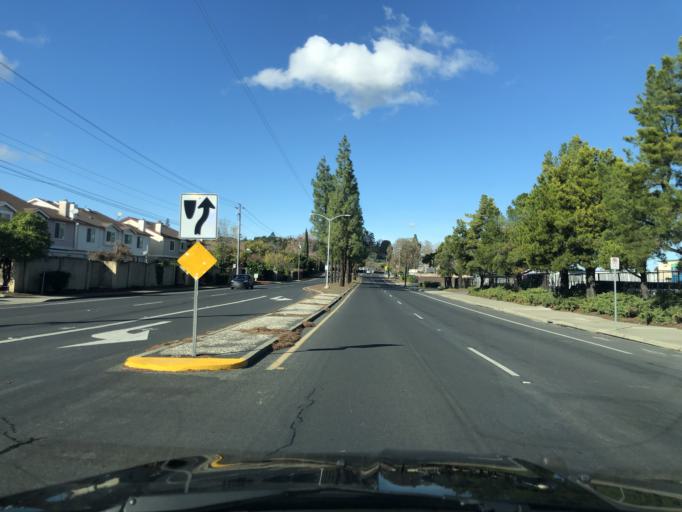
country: US
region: California
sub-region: Contra Costa County
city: Pacheco
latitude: 37.9880
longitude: -122.0712
